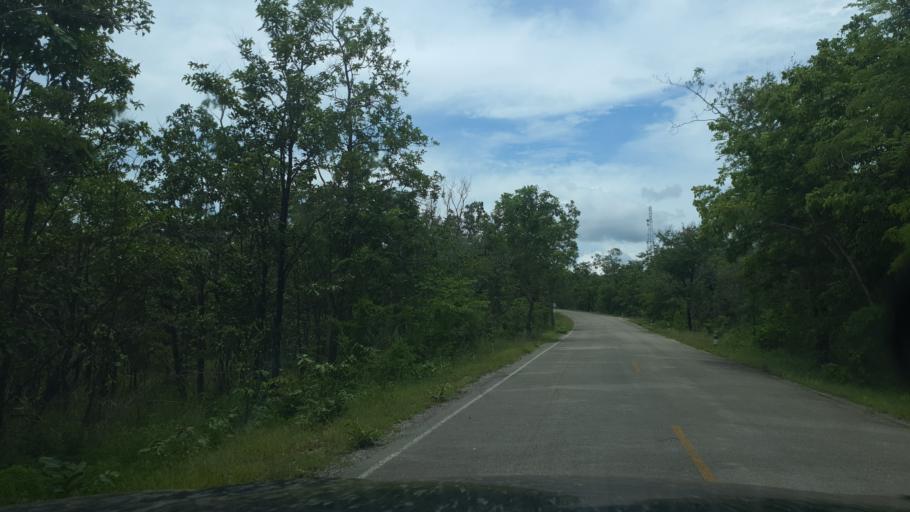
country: TH
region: Lampang
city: Soem Ngam
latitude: 18.0404
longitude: 99.3712
